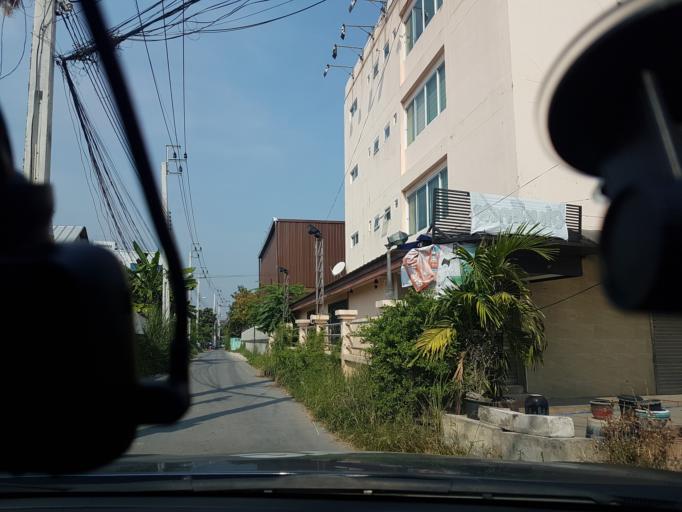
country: TH
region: Bangkok
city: Khan Na Yao
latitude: 13.8408
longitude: 100.6984
